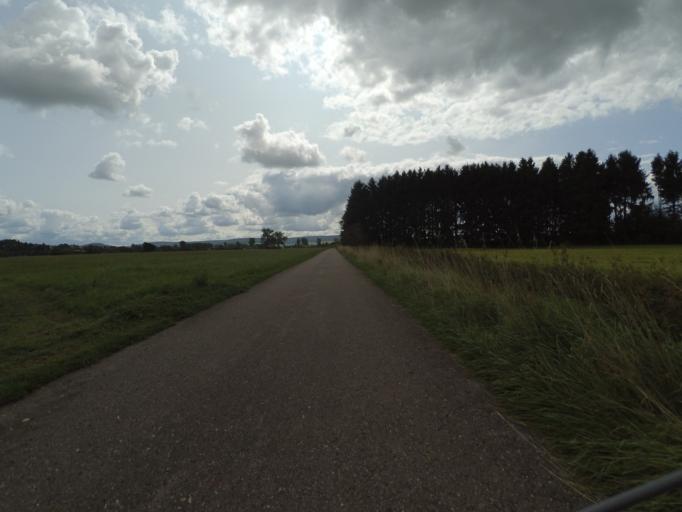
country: DE
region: Baden-Wuerttemberg
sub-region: Freiburg Region
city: Donaueschingen
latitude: 47.9451
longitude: 8.5340
